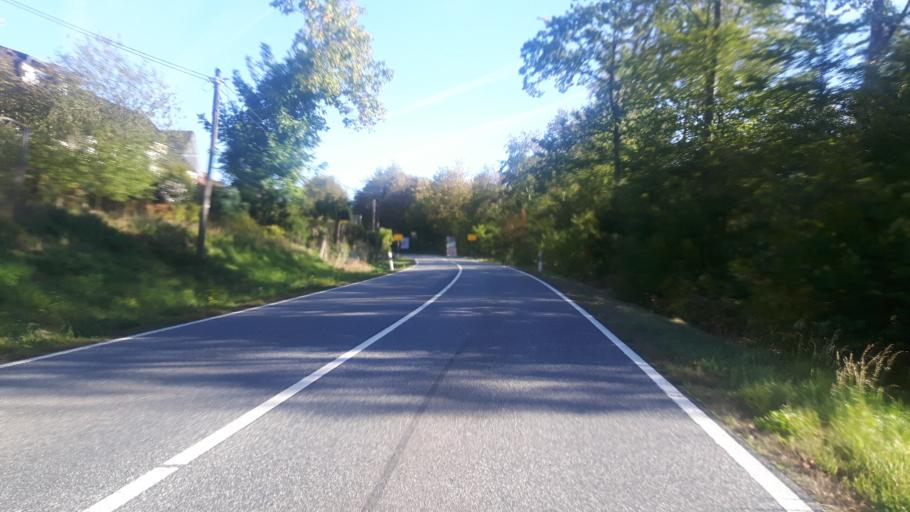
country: DE
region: Rheinland-Pfalz
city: Wallmenroth
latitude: 50.7962
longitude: 7.8297
